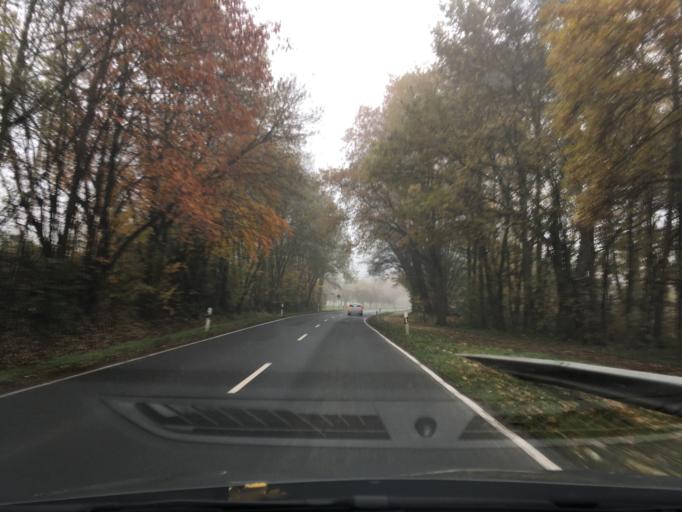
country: DE
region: North Rhine-Westphalia
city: Stadtlohn
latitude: 52.0682
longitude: 6.9277
